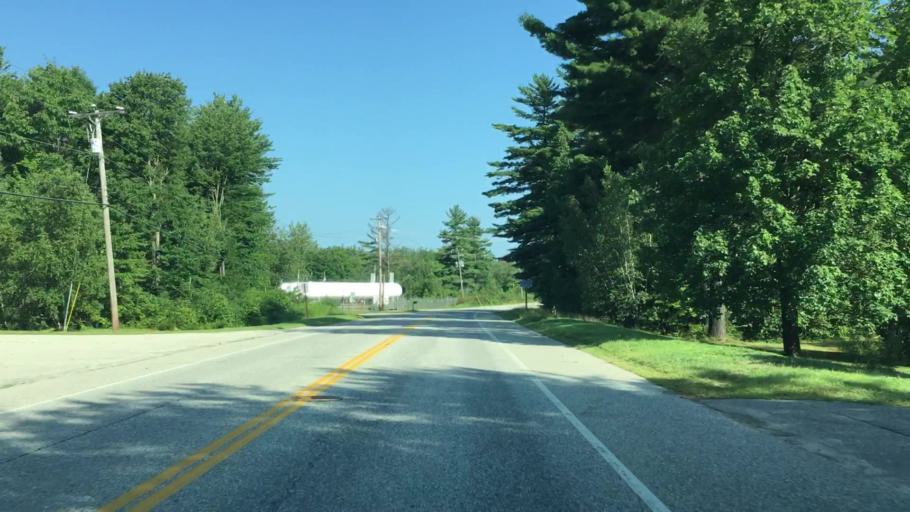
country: US
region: Maine
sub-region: Androscoggin County
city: Minot
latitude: 44.0452
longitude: -70.2946
